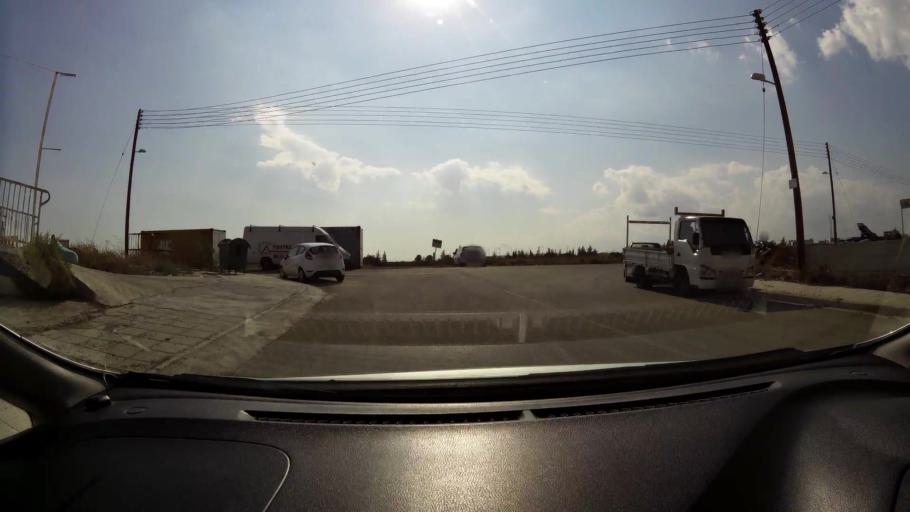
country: CY
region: Larnaka
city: Dhromolaxia
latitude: 34.9017
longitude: 33.5753
